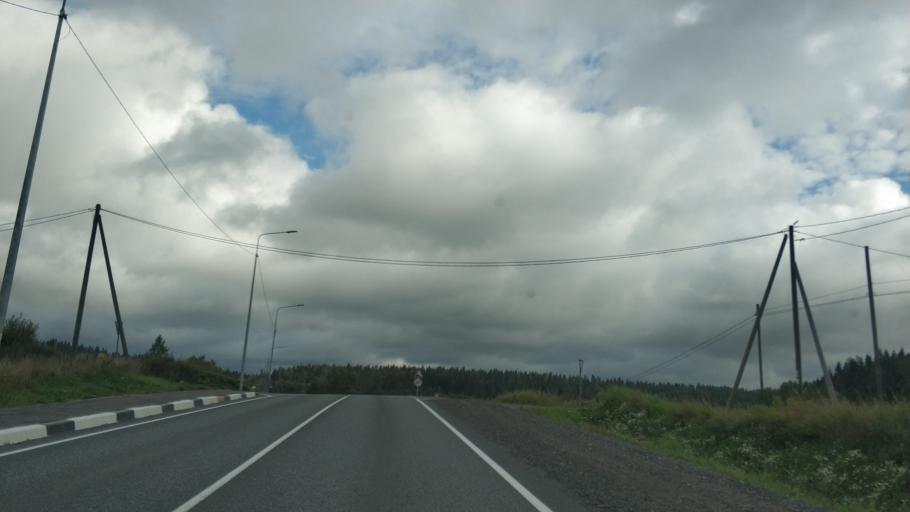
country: RU
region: Republic of Karelia
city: Khelyulya
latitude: 61.7586
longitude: 30.6572
